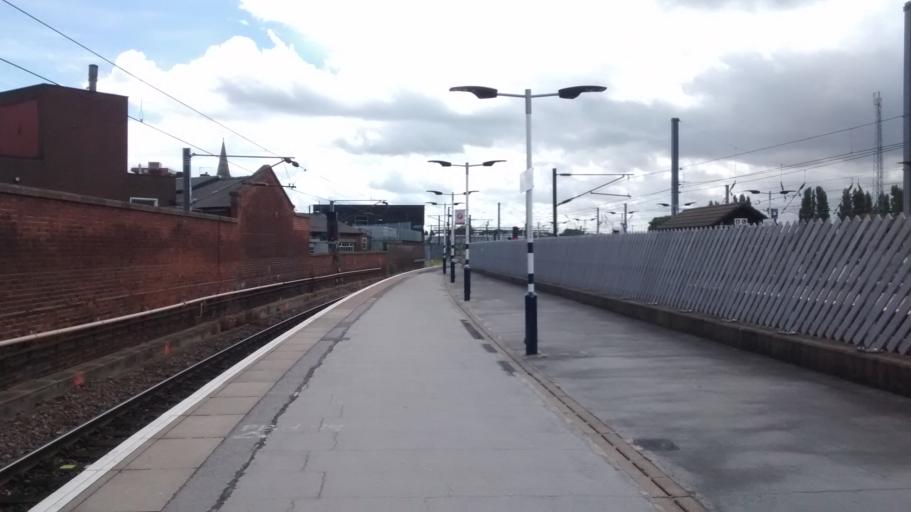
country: GB
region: England
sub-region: Doncaster
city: Doncaster
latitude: 53.5212
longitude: -1.1395
